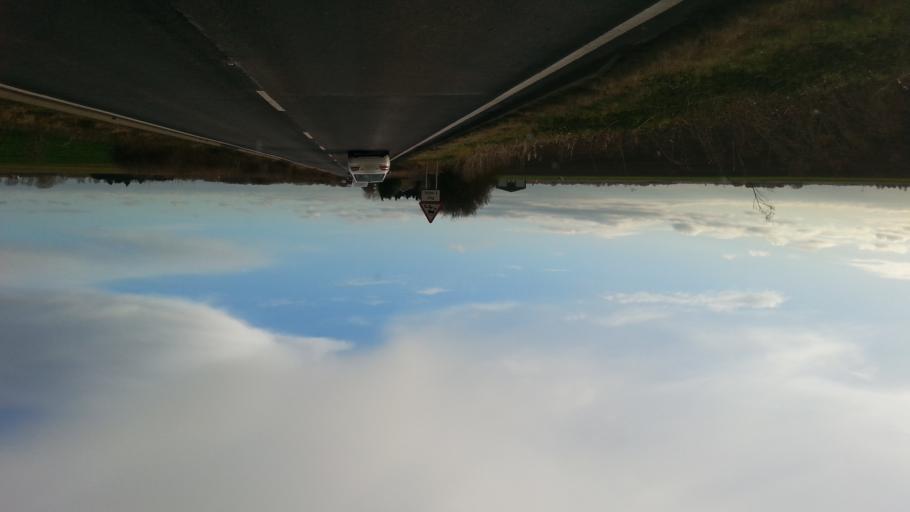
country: GB
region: England
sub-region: Peterborough
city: Thorney
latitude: 52.6192
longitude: -0.0406
